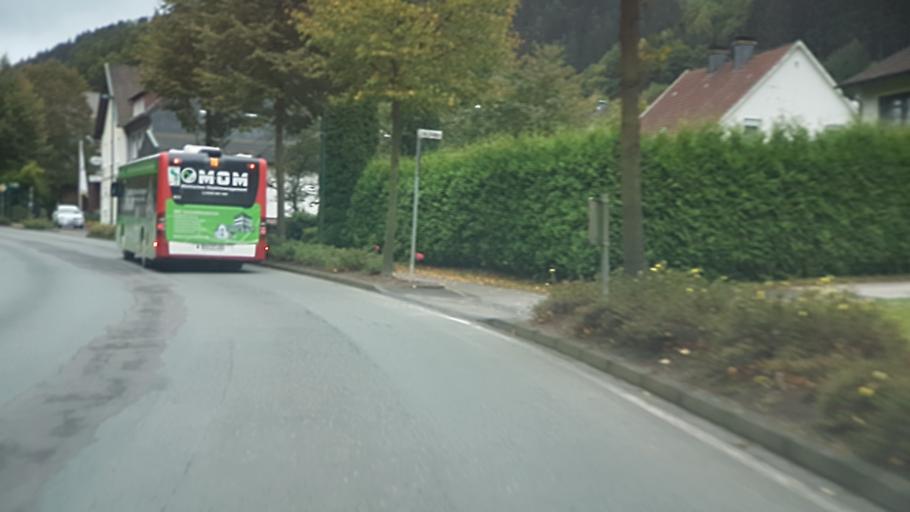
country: DE
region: North Rhine-Westphalia
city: Plettenberg
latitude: 51.1521
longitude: 7.8430
